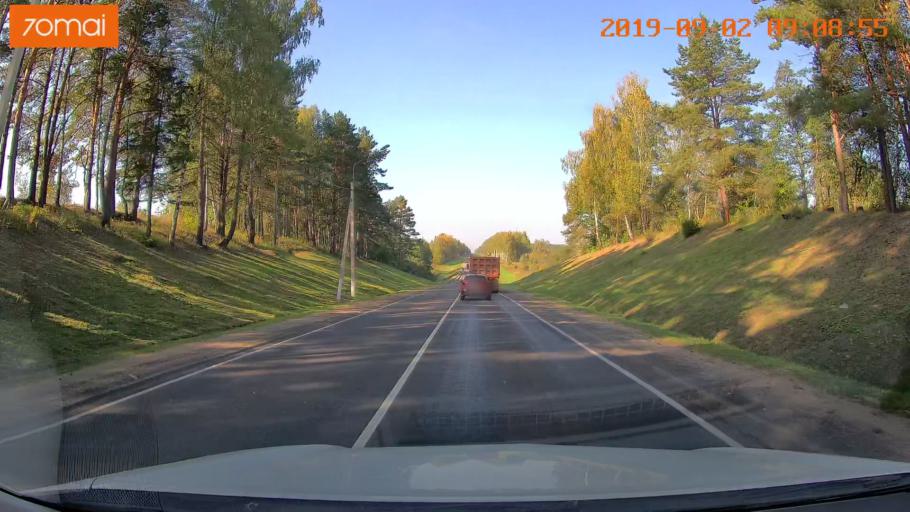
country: RU
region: Kaluga
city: Myatlevo
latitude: 54.8878
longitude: 35.6346
